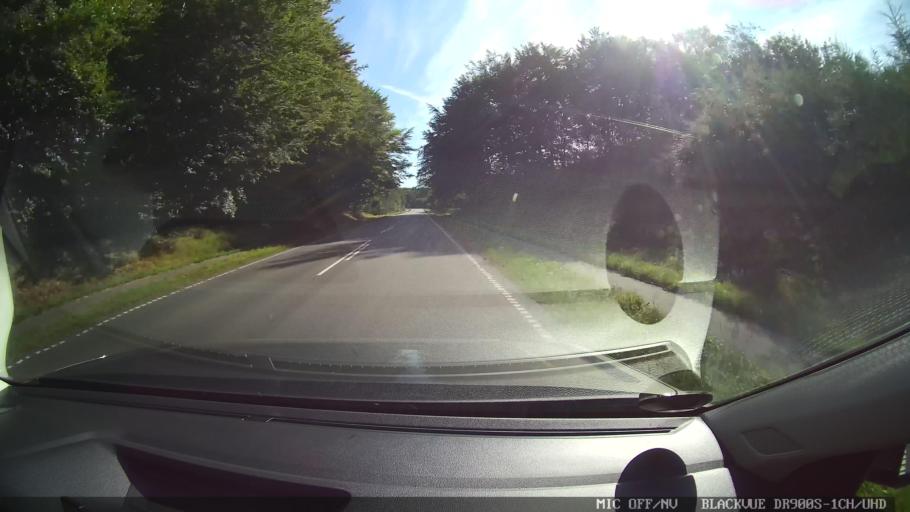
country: DK
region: North Denmark
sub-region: Mariagerfjord Kommune
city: Arden
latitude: 56.7738
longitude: 9.7848
